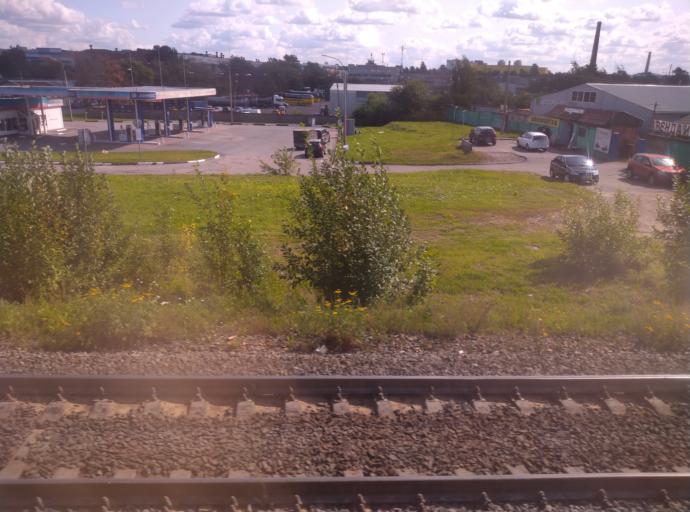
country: RU
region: St.-Petersburg
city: Centralniy
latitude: 59.9048
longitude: 30.3814
